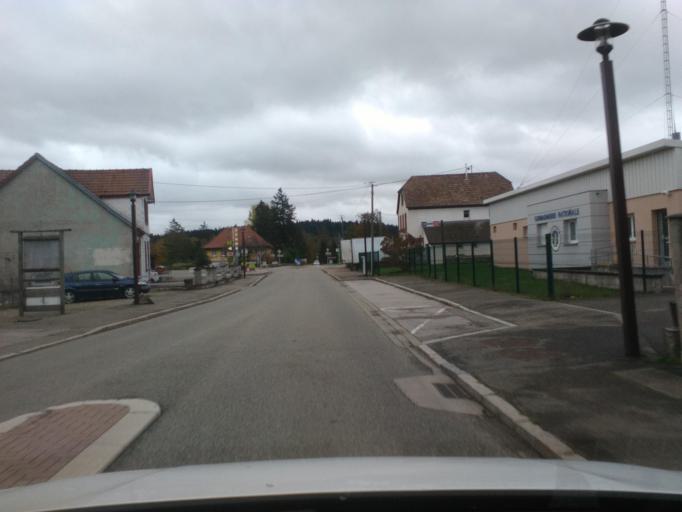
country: FR
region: Lorraine
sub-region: Departement des Vosges
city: Ban-de-Laveline
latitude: 48.3453
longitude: 7.1071
